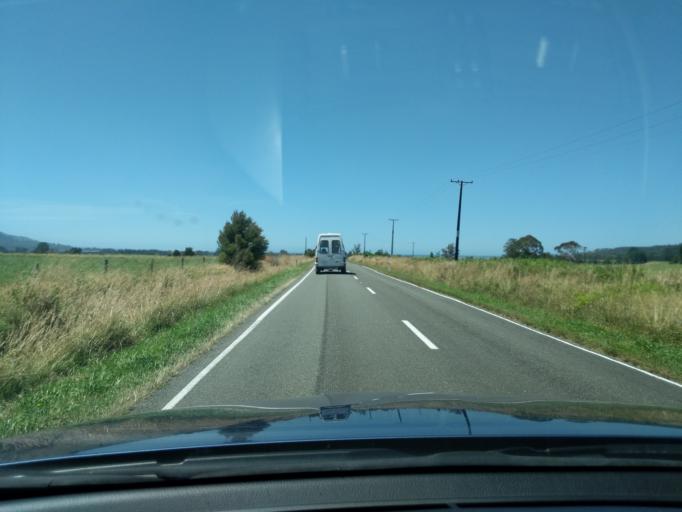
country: NZ
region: Tasman
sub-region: Tasman District
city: Takaka
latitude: -40.6891
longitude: 172.6466
